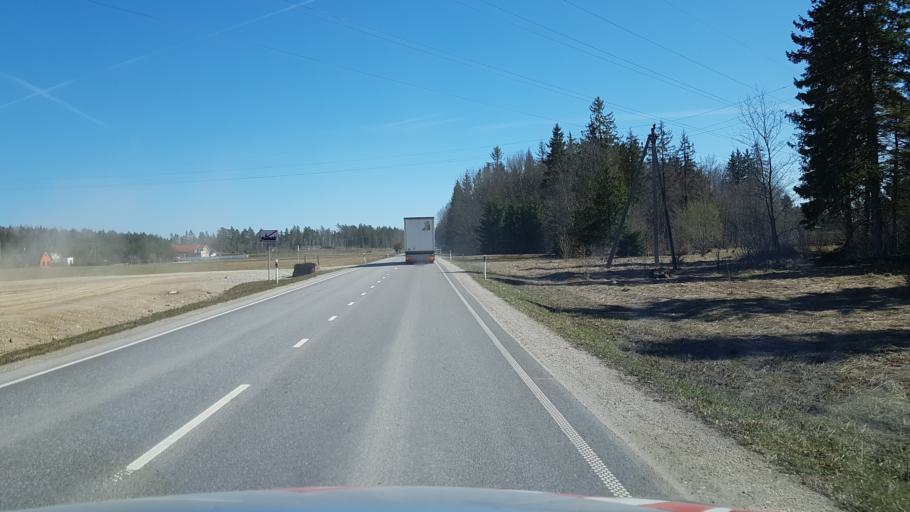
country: EE
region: Laeaene-Virumaa
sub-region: Rakvere linn
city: Rakvere
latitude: 59.3353
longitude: 26.3946
